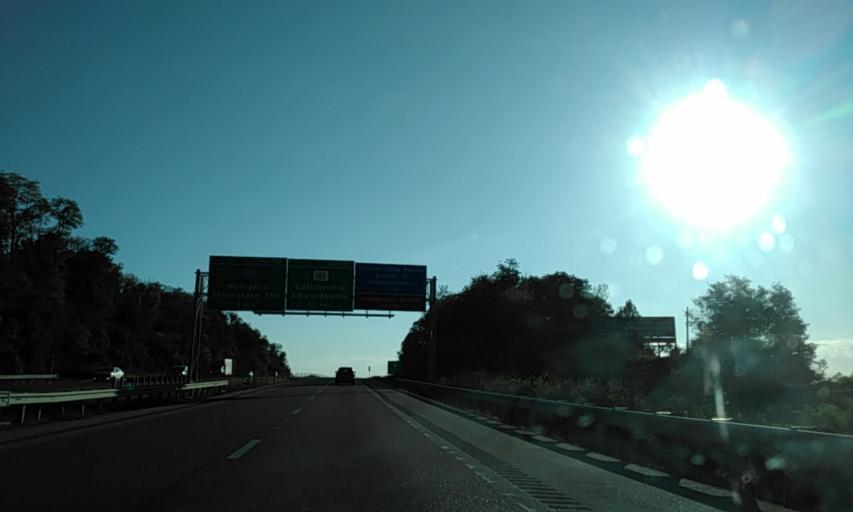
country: US
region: Illinois
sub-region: Madison County
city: Collinsville
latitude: 38.6862
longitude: -90.0060
